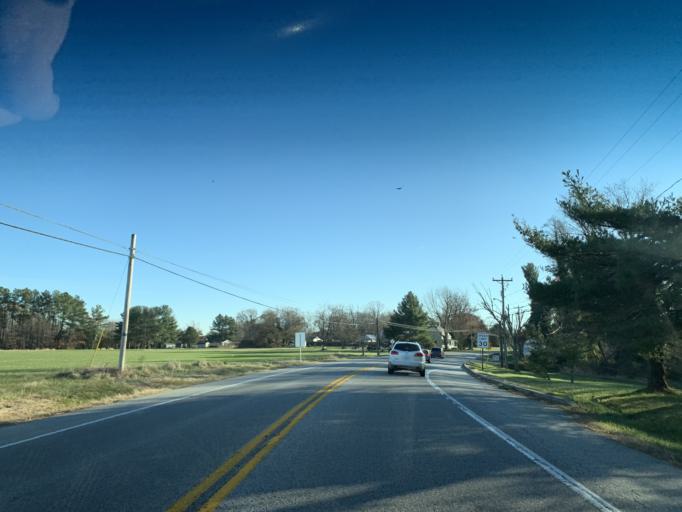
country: US
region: Delaware
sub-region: New Castle County
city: Middletown
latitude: 39.3707
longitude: -75.8831
